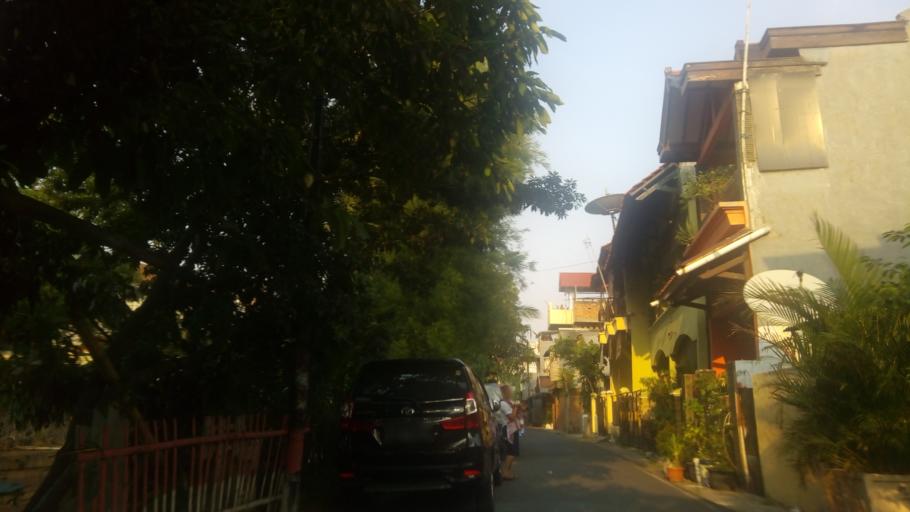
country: ID
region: Jakarta Raya
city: Jakarta
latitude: -6.2023
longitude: 106.8536
